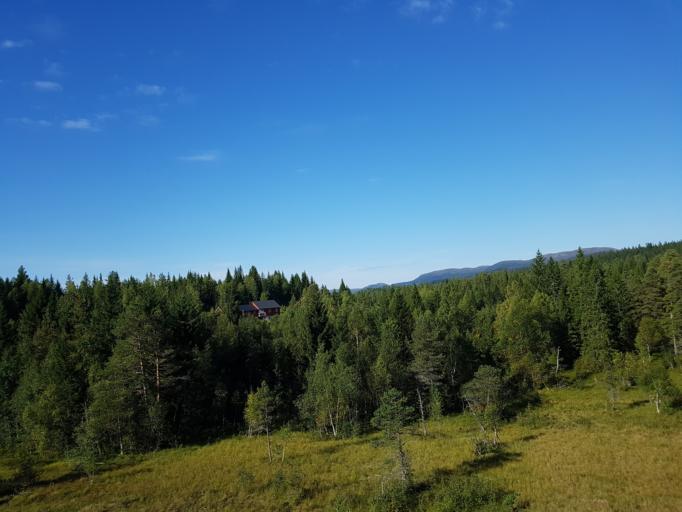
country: NO
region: Sor-Trondelag
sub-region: Trondheim
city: Trondheim
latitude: 63.6434
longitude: 10.2696
